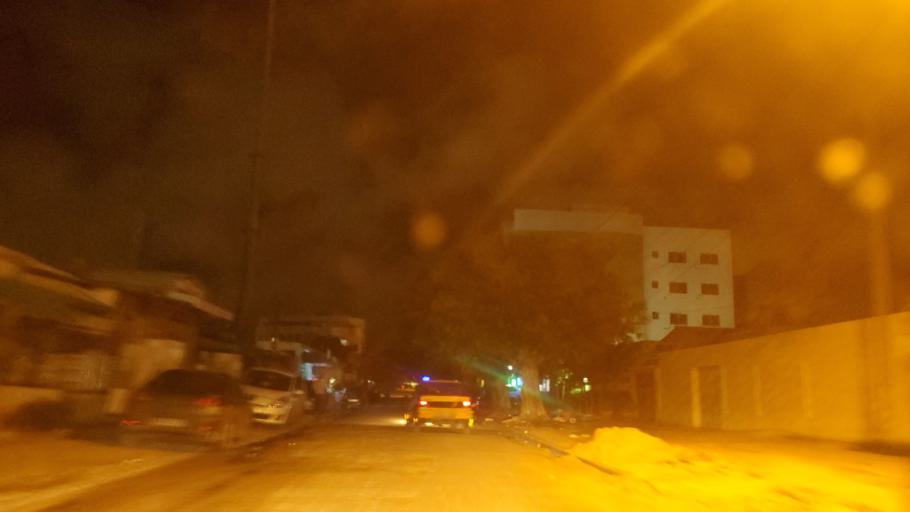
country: SN
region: Dakar
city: Grand Dakar
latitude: 14.7113
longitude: -17.4571
